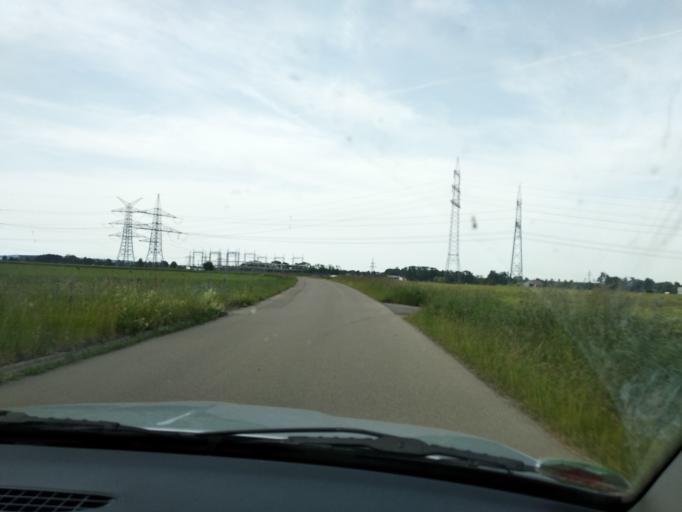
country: DE
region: Bavaria
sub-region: Swabia
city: Woringen
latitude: 47.9325
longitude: 10.2112
